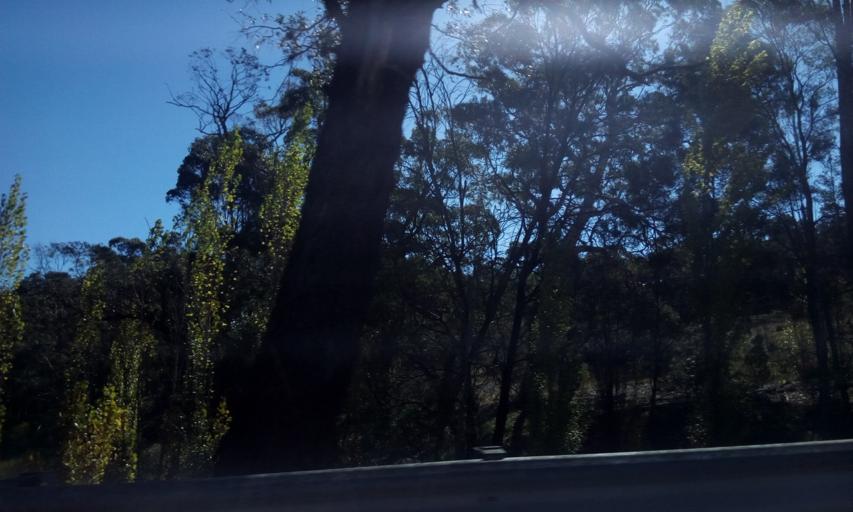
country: AU
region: New South Wales
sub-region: Wingecarribee
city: Bundanoon
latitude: -34.6410
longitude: 150.1249
